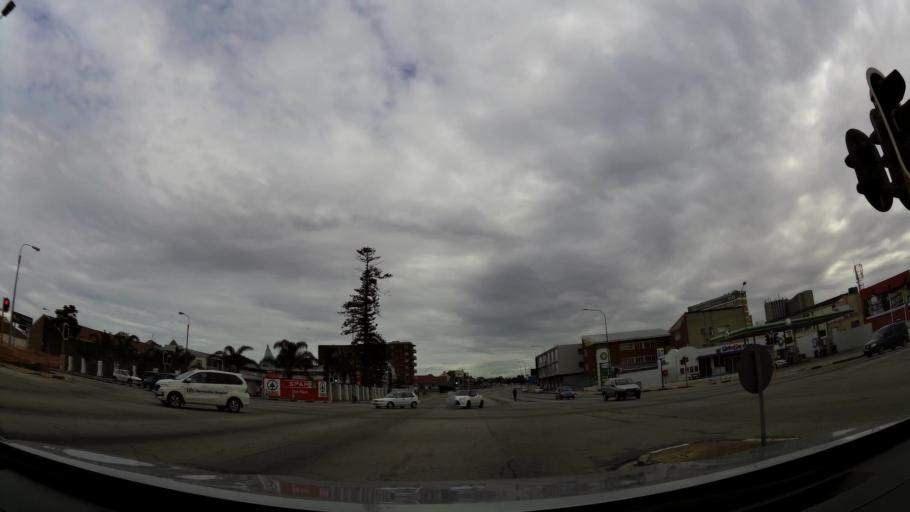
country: ZA
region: Eastern Cape
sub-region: Nelson Mandela Bay Metropolitan Municipality
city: Port Elizabeth
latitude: -33.9610
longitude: 25.6025
